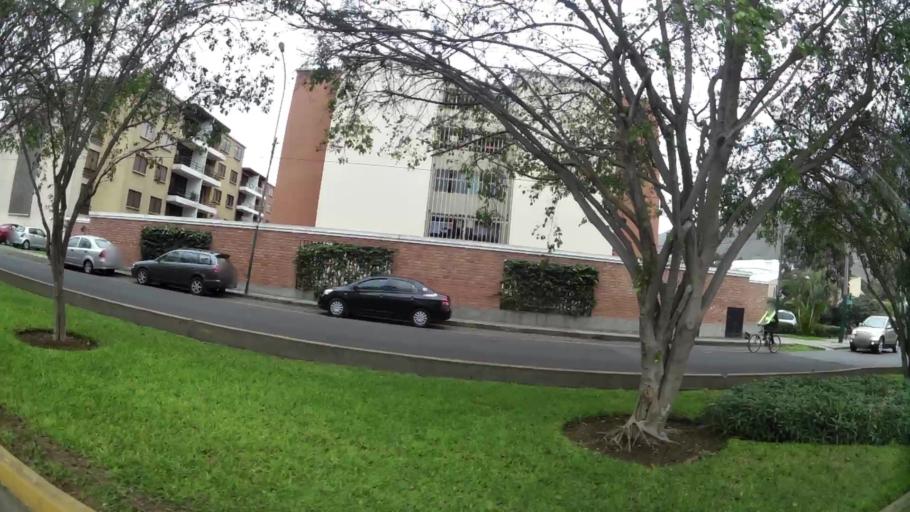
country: PE
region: Lima
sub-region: Lima
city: La Molina
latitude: -12.1081
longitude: -76.9638
